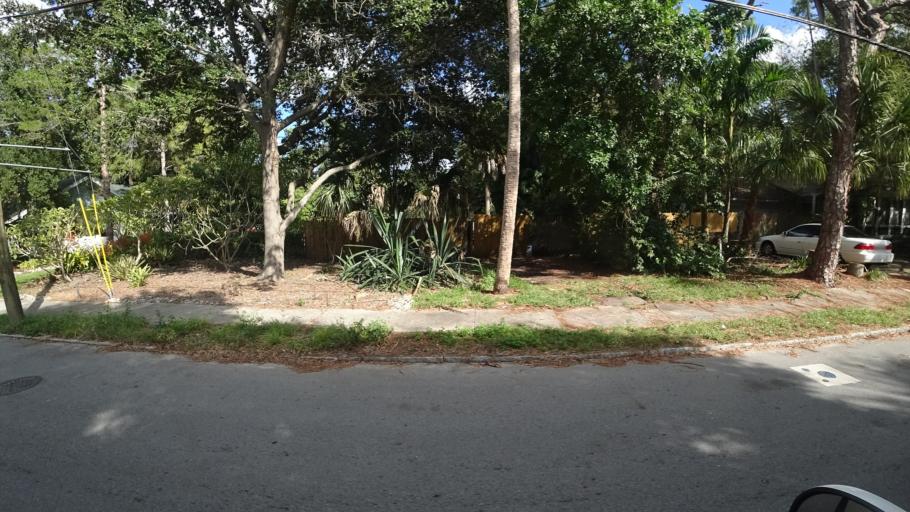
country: US
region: Florida
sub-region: Manatee County
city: Bradenton
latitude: 27.4900
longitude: -82.5835
